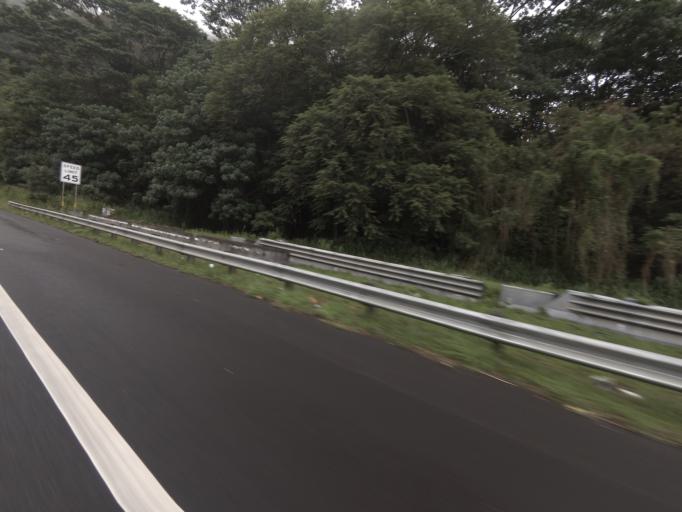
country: US
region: Hawaii
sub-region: Honolulu County
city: Kane'ohe
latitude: 21.3931
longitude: -157.8141
